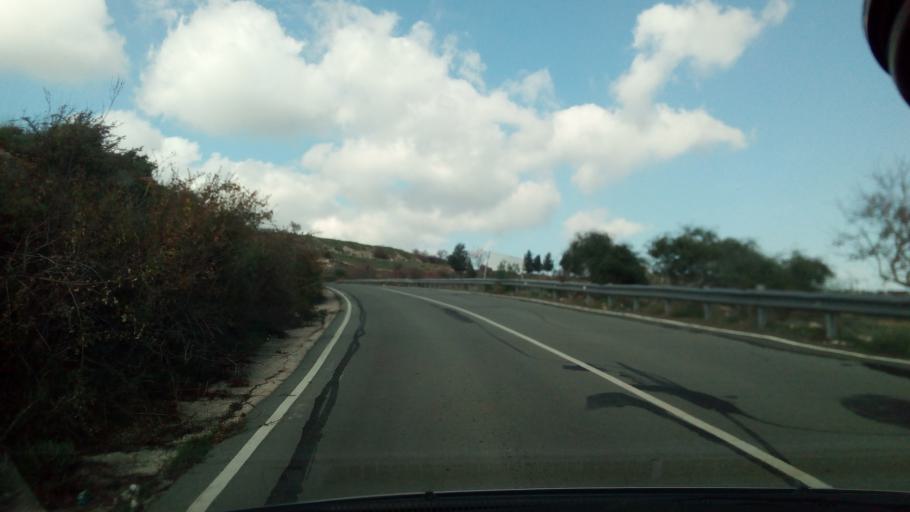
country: CY
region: Pafos
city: Pegeia
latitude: 34.9558
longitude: 32.4141
